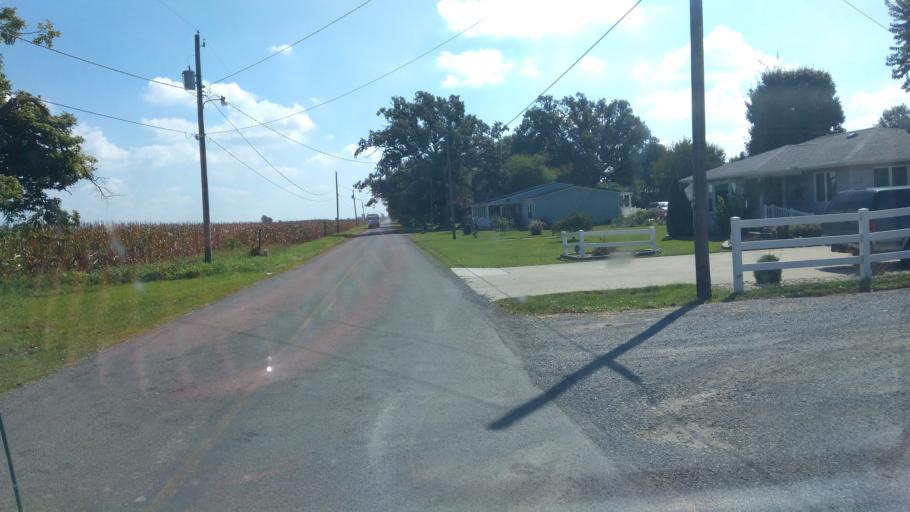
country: US
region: Ohio
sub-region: Hardin County
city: Ada
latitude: 40.7032
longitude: -83.8422
